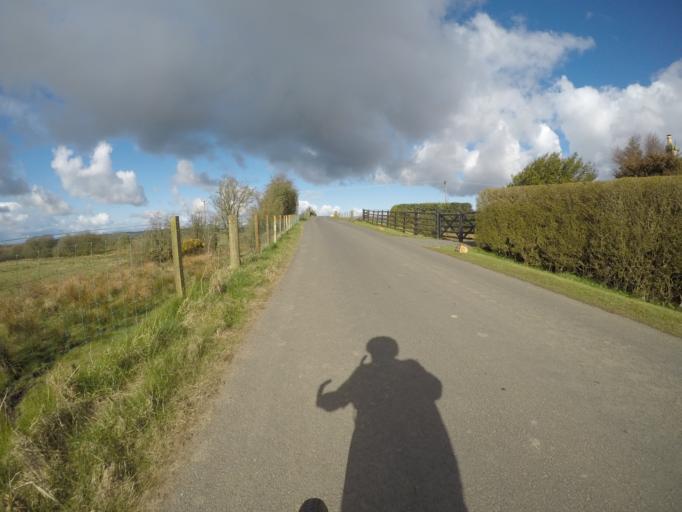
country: GB
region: Scotland
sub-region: North Ayrshire
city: Kilwinning
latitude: 55.6875
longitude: -4.6612
